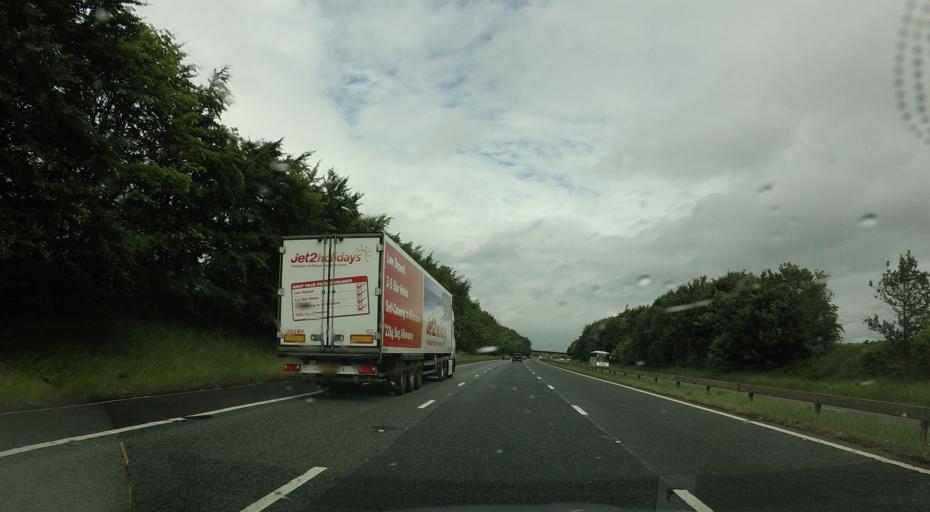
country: GB
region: England
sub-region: Cumbria
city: Scotby
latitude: 54.8139
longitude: -2.8826
